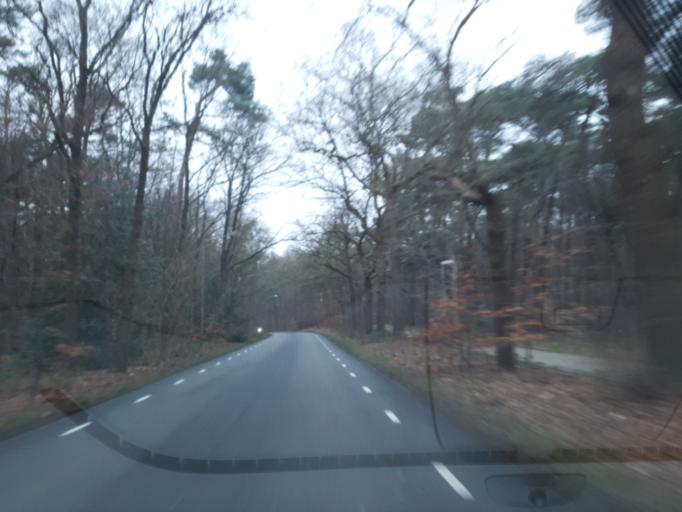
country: NL
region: North Holland
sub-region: Gemeente Wijdemeren
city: Nieuw-Loosdrecht
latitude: 52.1878
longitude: 5.1696
